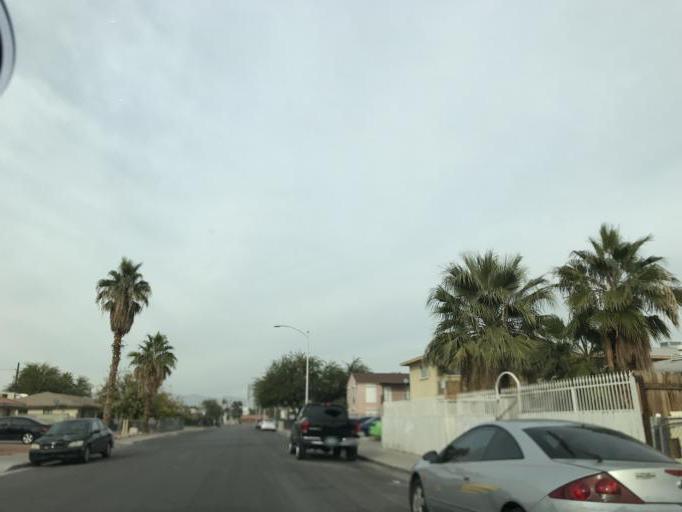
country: US
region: Nevada
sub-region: Clark County
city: Las Vegas
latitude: 36.1488
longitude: -115.1511
